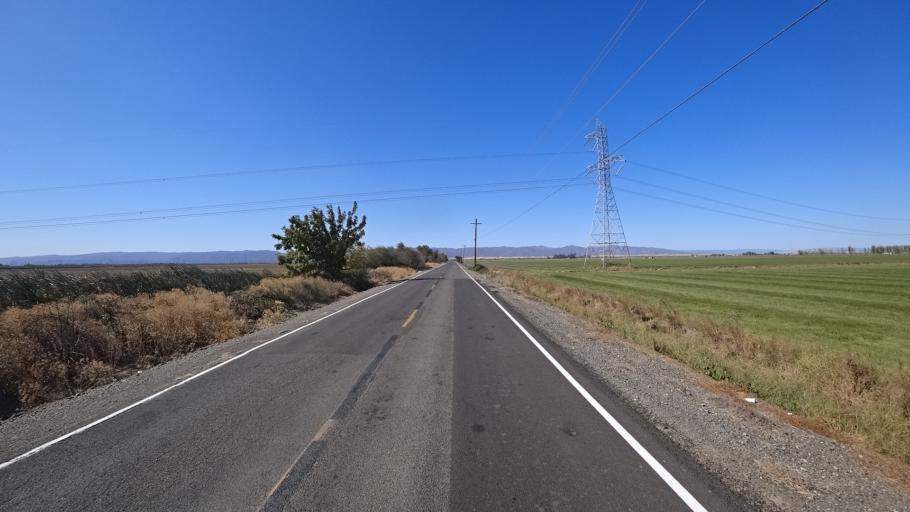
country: US
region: California
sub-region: Yolo County
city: Winters
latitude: 38.5619
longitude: -121.9079
